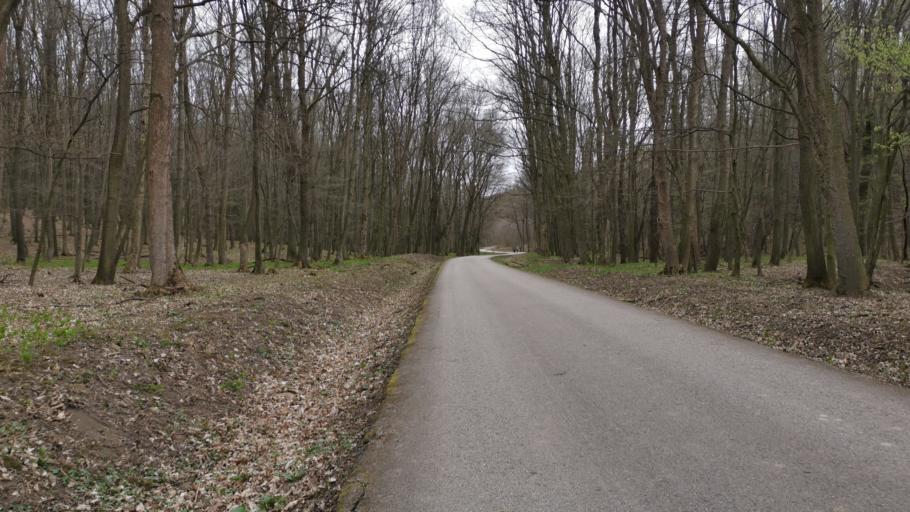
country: CZ
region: South Moravian
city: Sudomerice
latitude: 48.8222
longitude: 17.3023
